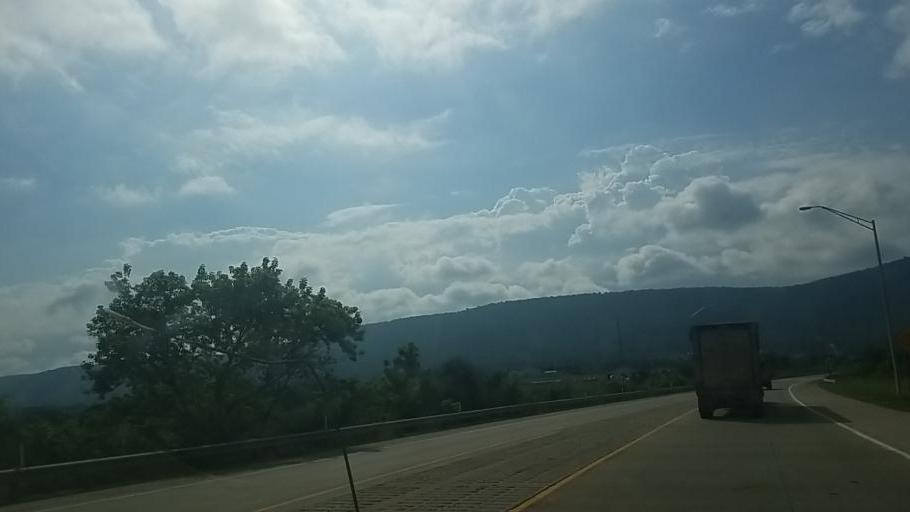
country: US
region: Pennsylvania
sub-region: Centre County
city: Pleasant Gap
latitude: 40.8870
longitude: -77.7268
